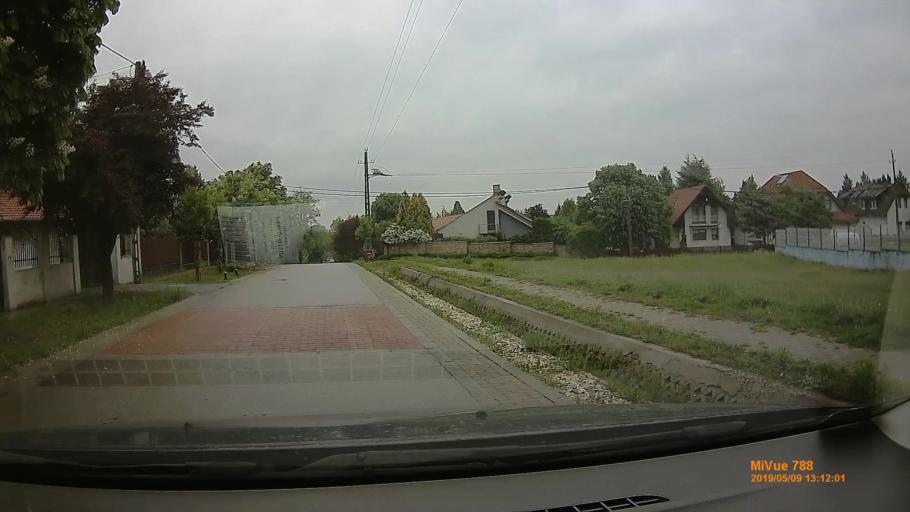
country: HU
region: Budapest
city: Budapest XVI. keruelet
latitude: 47.5387
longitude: 19.1855
